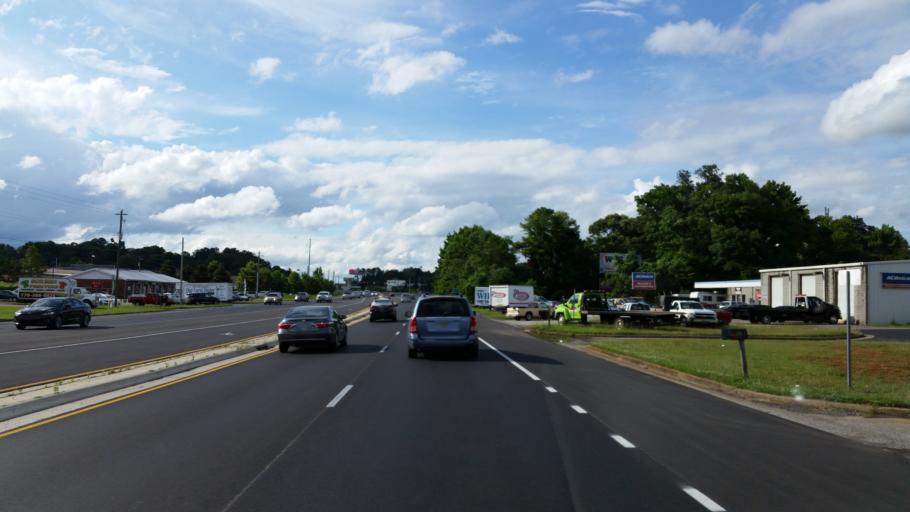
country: US
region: Georgia
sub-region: Bartow County
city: Cartersville
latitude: 34.1834
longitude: -84.7854
